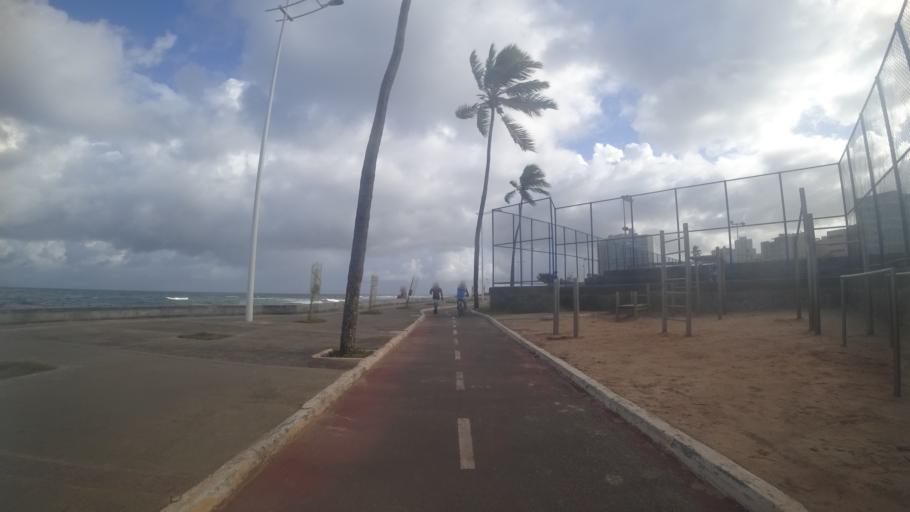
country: BR
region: Bahia
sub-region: Salvador
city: Salvador
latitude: -13.0024
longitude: -38.4502
